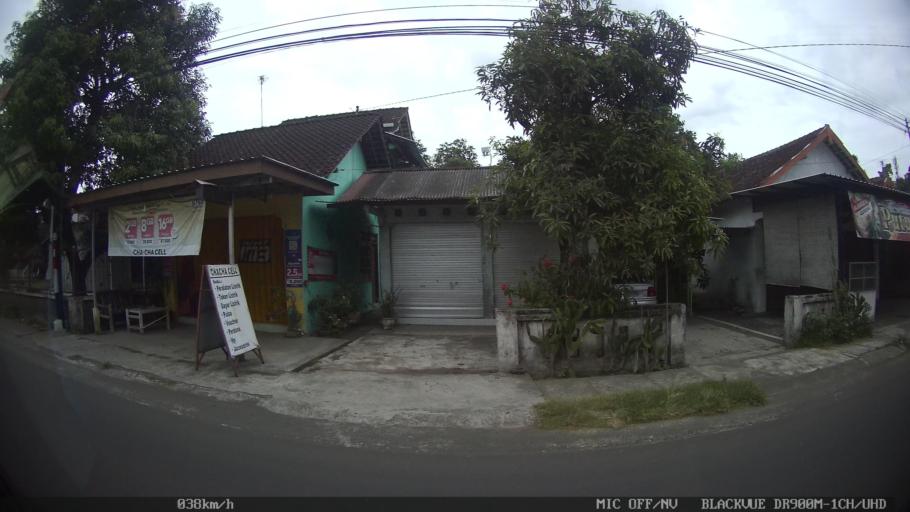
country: ID
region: Daerah Istimewa Yogyakarta
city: Sewon
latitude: -7.8786
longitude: 110.4131
